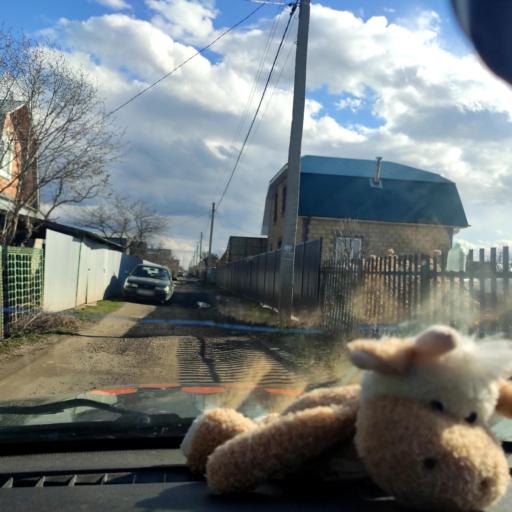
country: RU
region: Samara
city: Tol'yatti
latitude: 53.5969
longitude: 49.3092
